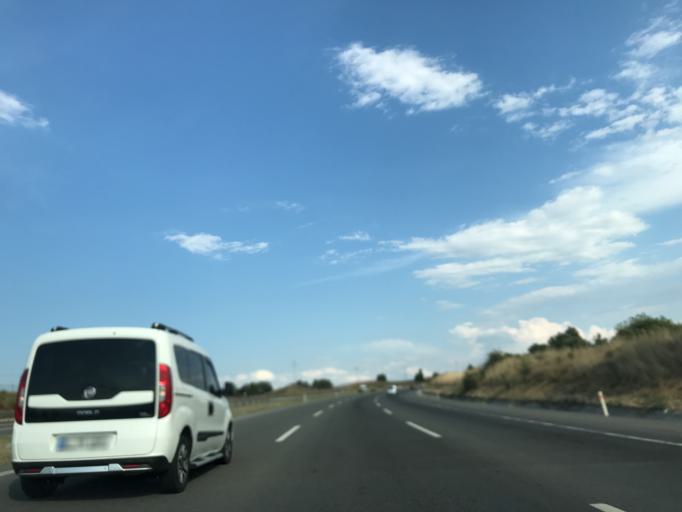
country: TR
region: Bolu
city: Yenicaga
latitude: 40.7646
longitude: 32.0546
